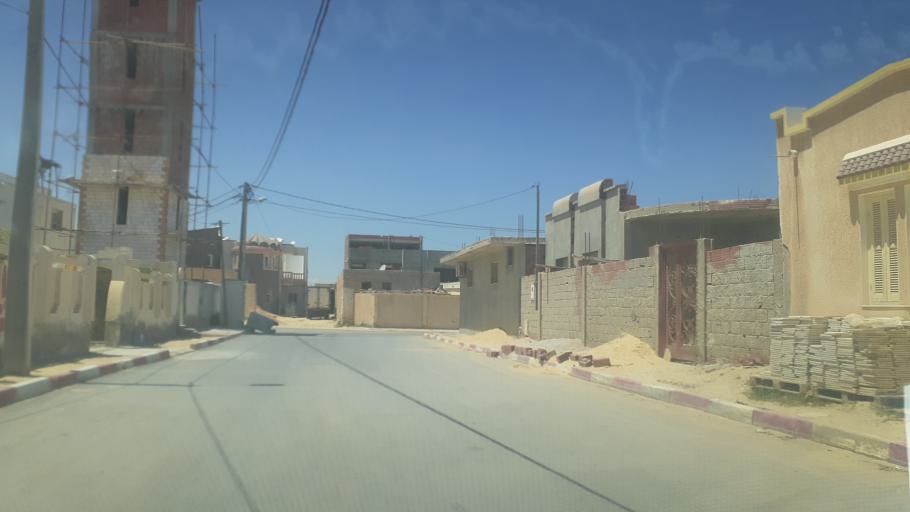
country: TN
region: Qabis
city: Gabes
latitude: 33.9331
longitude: 10.0607
